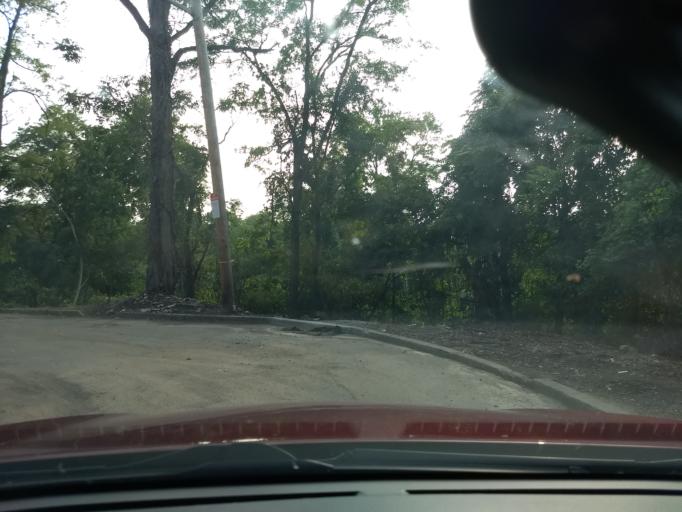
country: US
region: Pennsylvania
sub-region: Allegheny County
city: Aspinwall
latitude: 40.4668
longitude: -79.9068
